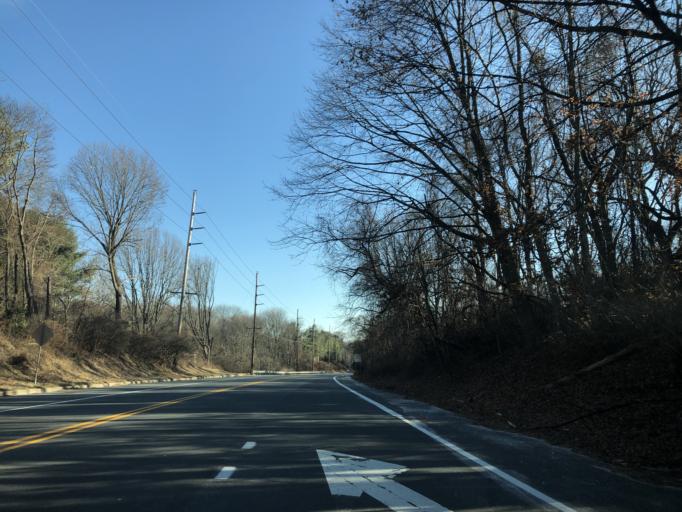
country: US
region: Delaware
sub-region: New Castle County
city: Hockessin
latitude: 39.7847
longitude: -75.6844
